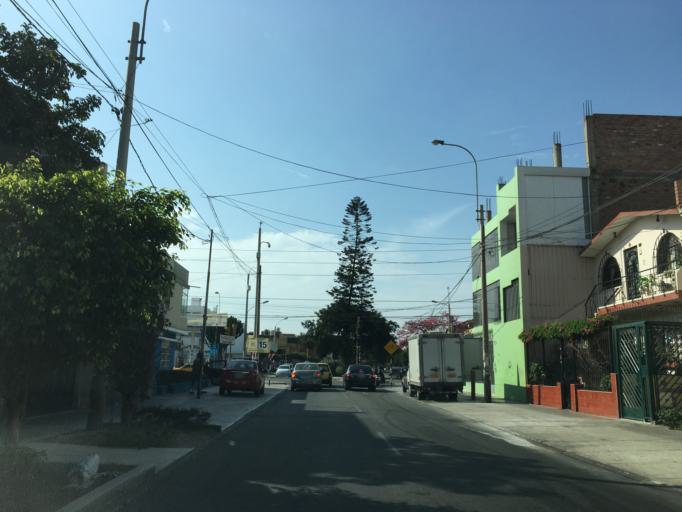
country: PE
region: Lima
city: Lima
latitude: -12.0682
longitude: -77.0675
